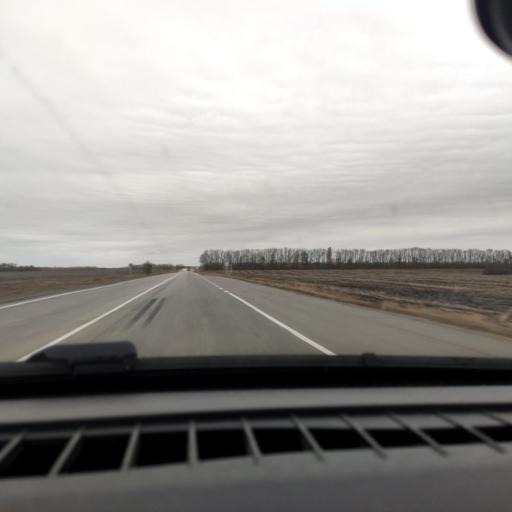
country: RU
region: Voronezj
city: Strelitsa
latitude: 51.5120
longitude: 38.9669
